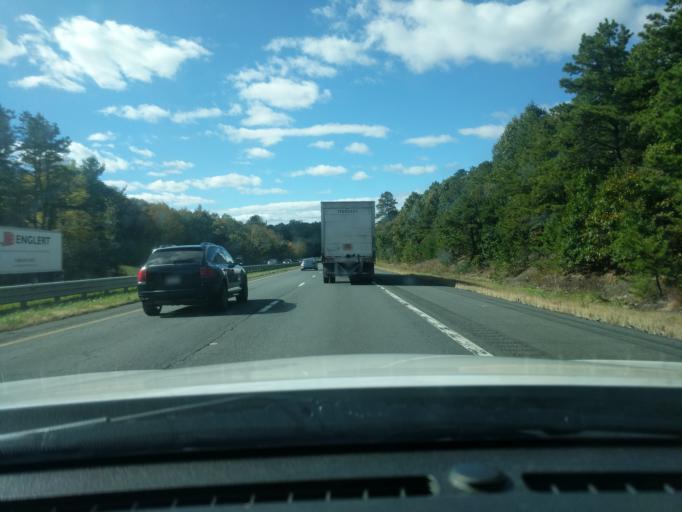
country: US
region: Massachusetts
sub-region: Hampden County
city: Westfield
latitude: 42.1399
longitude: -72.7079
